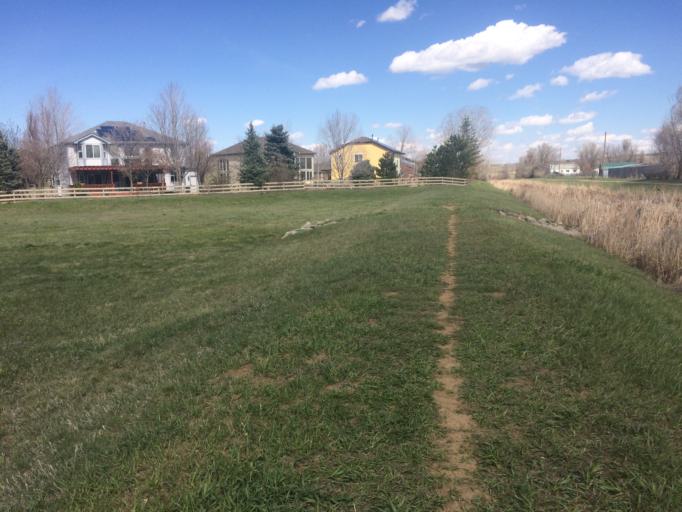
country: US
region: Colorado
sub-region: Boulder County
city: Lafayette
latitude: 39.9655
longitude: -105.0970
